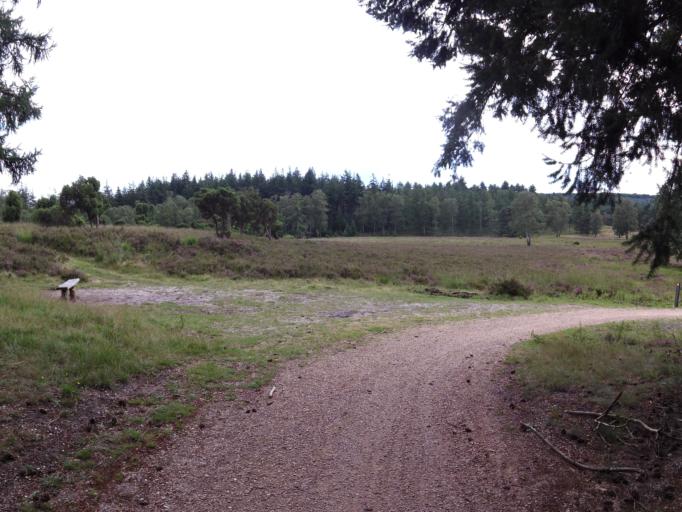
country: NL
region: Gelderland
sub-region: Gemeente Apeldoorn
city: Loenen
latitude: 52.0875
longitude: 5.9898
